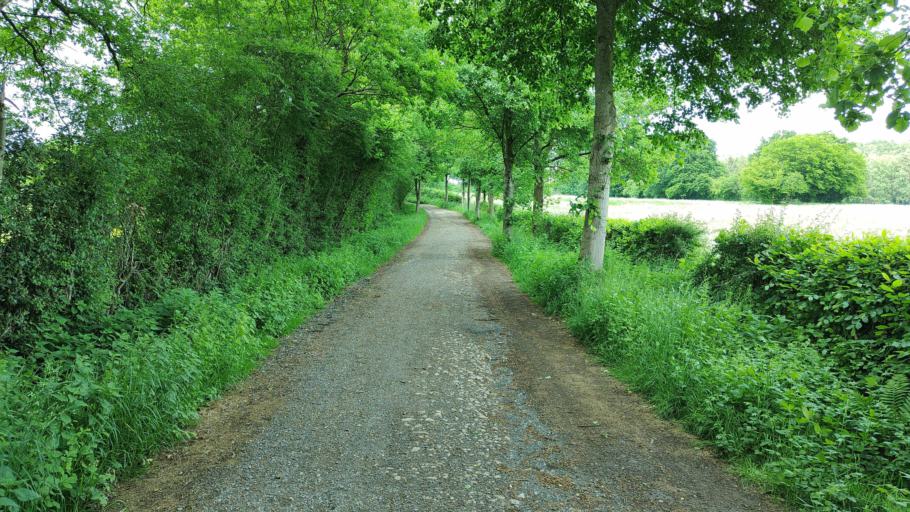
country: BE
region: Wallonia
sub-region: Province de Liege
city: La Calamine
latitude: 50.7153
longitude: 6.0676
